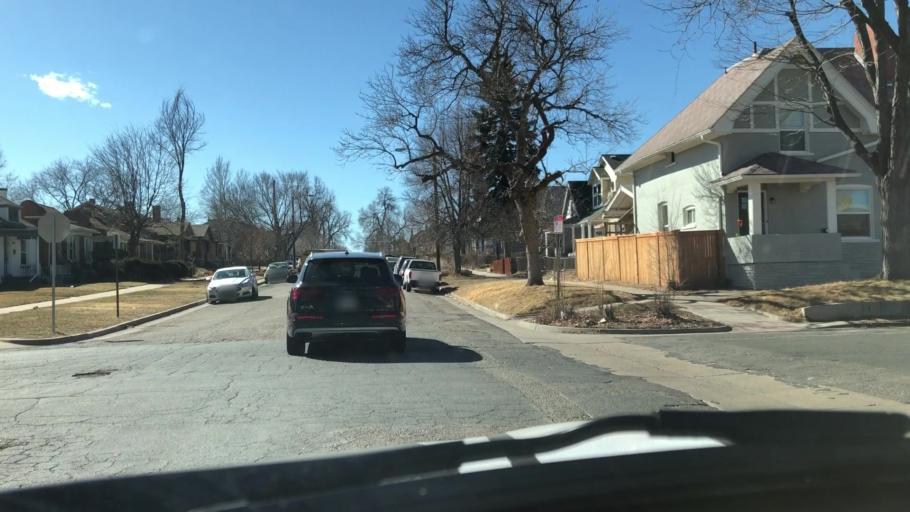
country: US
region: Colorado
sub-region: Denver County
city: Denver
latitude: 39.7559
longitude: -104.9649
